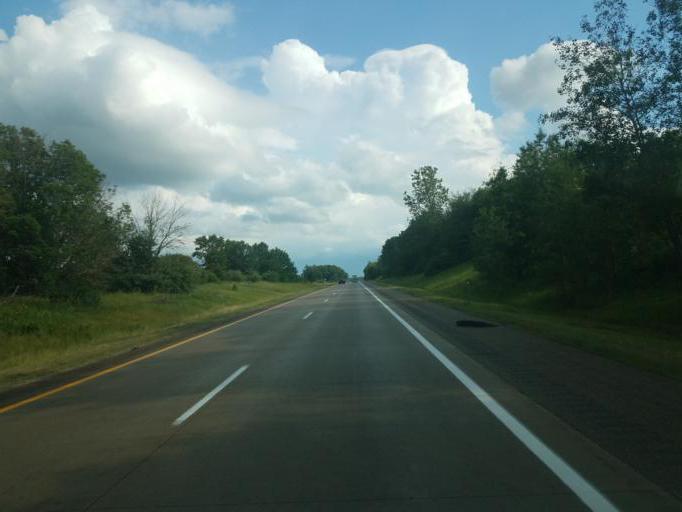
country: US
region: Michigan
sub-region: Calhoun County
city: Marshall
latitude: 42.2159
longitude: -84.9824
